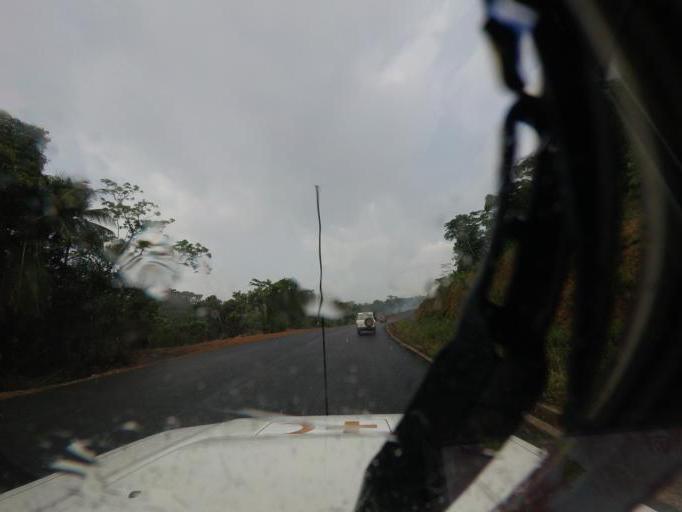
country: LR
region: Margibi
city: Kakata
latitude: 6.7763
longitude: -10.0011
